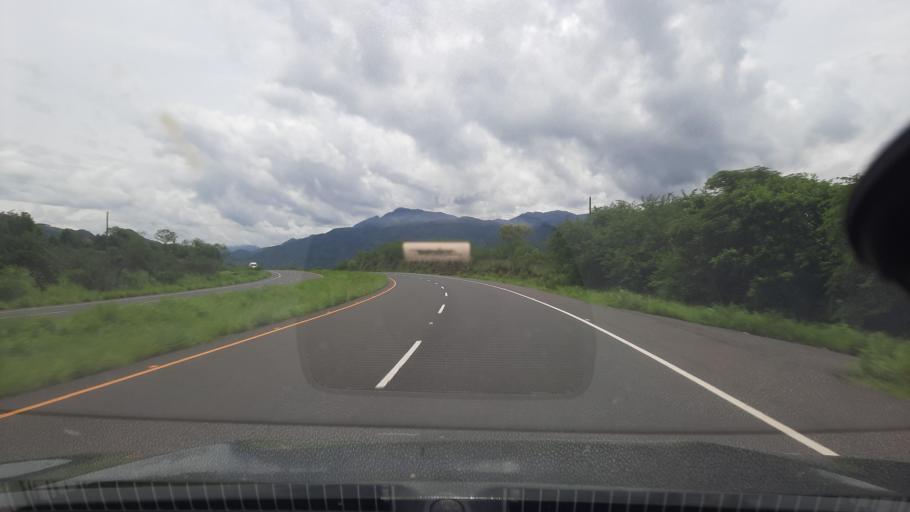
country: HN
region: Valle
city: Aramecina
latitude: 13.7694
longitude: -87.7032
